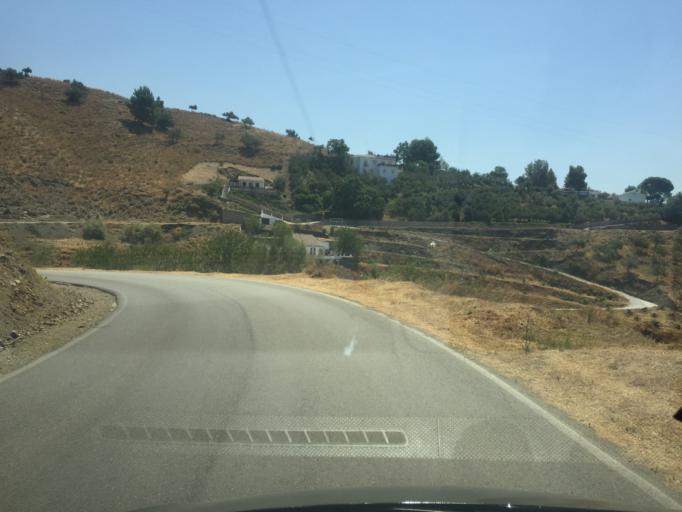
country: ES
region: Andalusia
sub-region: Provincia de Malaga
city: Frigiliana
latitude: 36.8045
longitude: -3.9214
